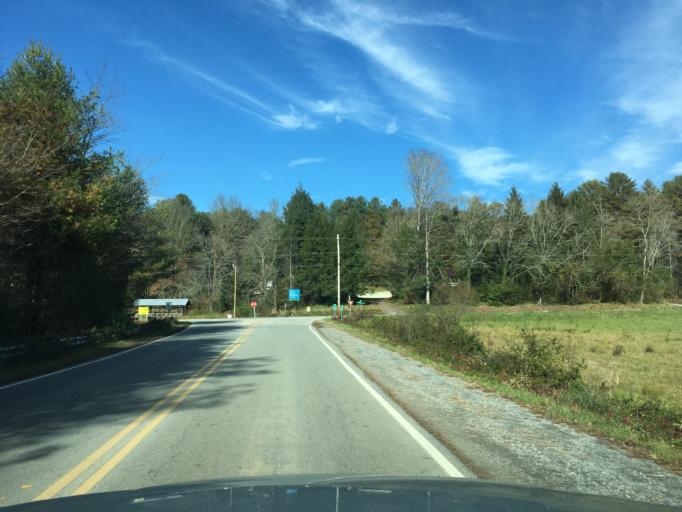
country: US
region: North Carolina
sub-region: Henderson County
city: Etowah
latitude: 35.2365
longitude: -82.6003
